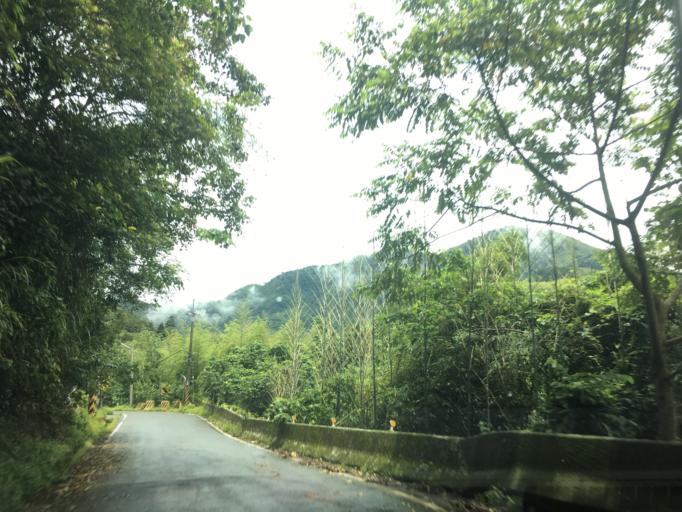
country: TW
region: Taiwan
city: Lugu
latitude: 23.5493
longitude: 120.6809
